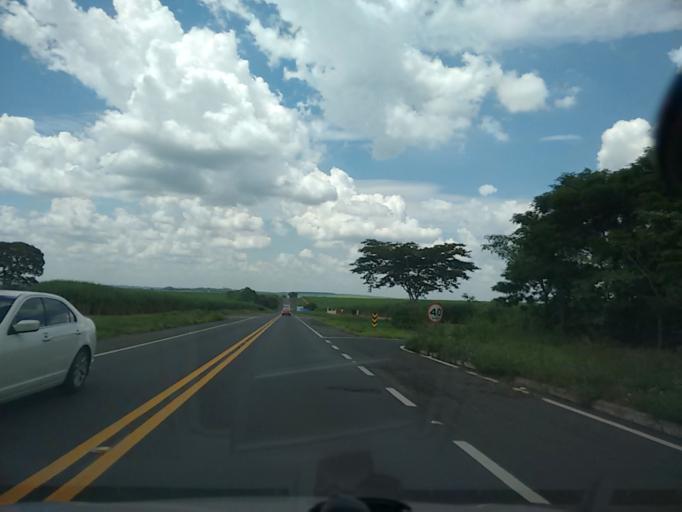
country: BR
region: Sao Paulo
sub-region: Osvaldo Cruz
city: Osvaldo Cruz
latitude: -21.9079
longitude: -50.8887
